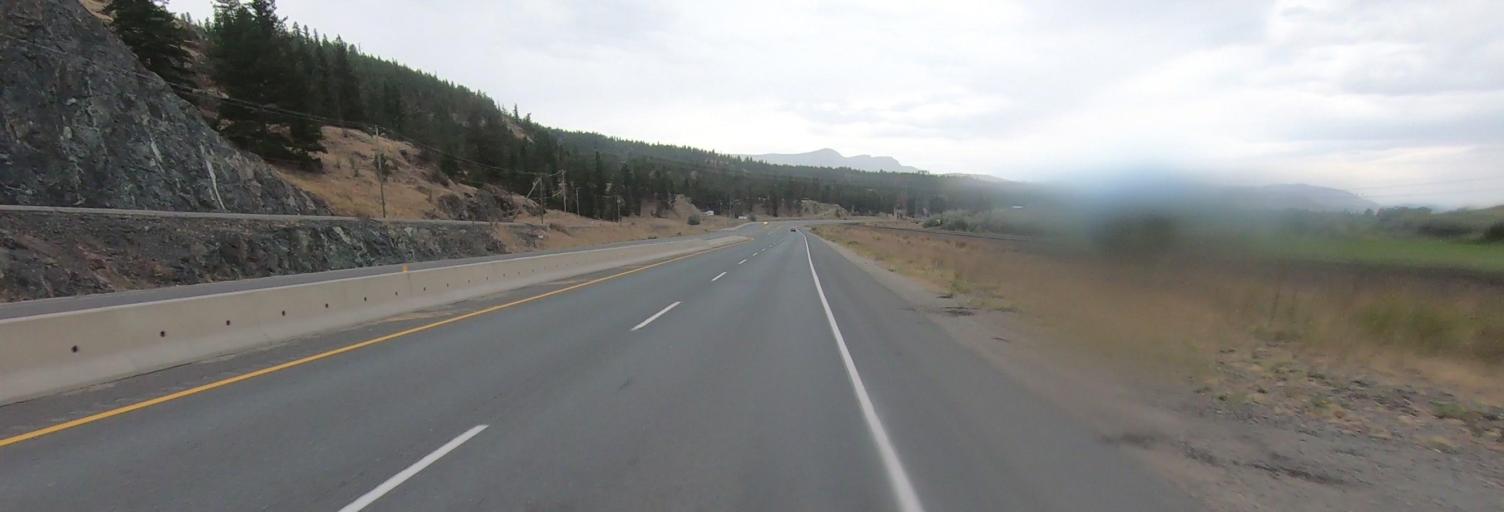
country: CA
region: British Columbia
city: Chase
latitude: 50.6490
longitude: -119.8991
